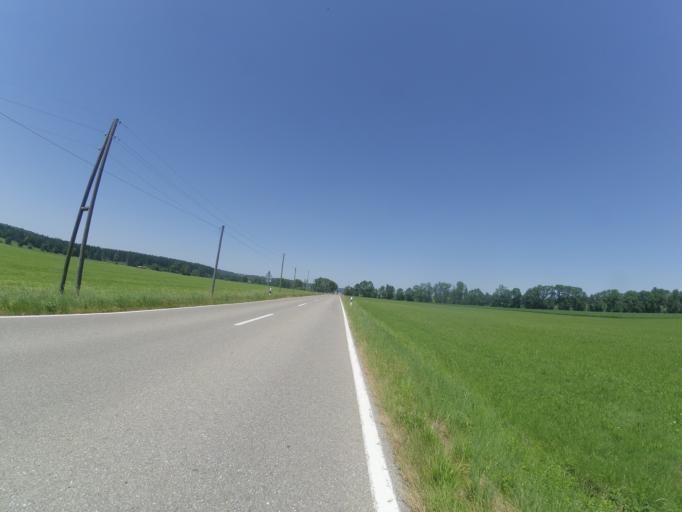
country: DE
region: Bavaria
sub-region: Swabia
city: Bohen
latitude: 47.8940
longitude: 10.3229
